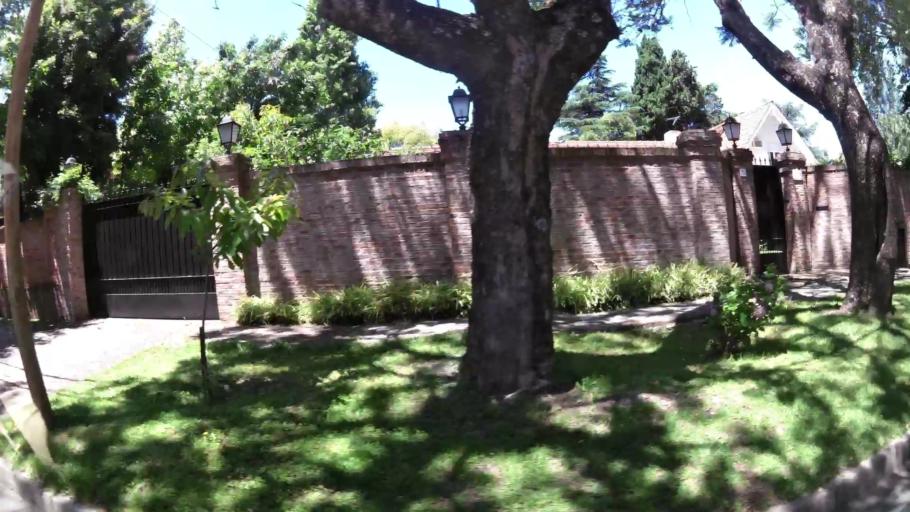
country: AR
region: Buenos Aires
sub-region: Partido de San Isidro
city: San Isidro
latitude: -34.4986
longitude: -58.5625
